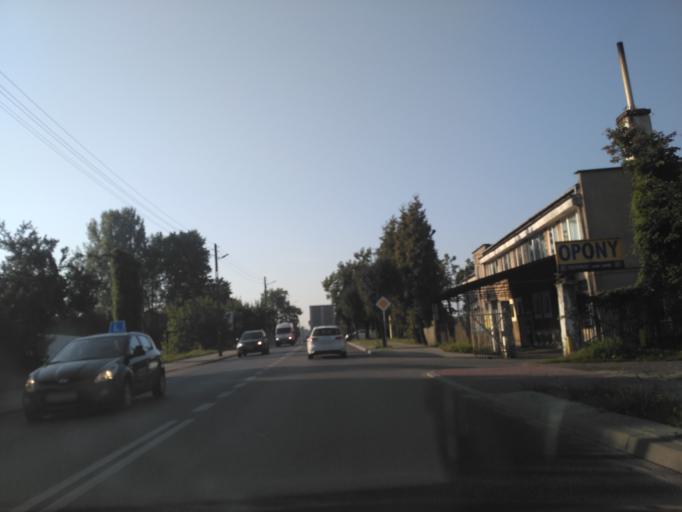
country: PL
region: Lublin Voivodeship
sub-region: Powiat janowski
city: Janow Lubelski
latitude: 50.7100
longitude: 22.4065
